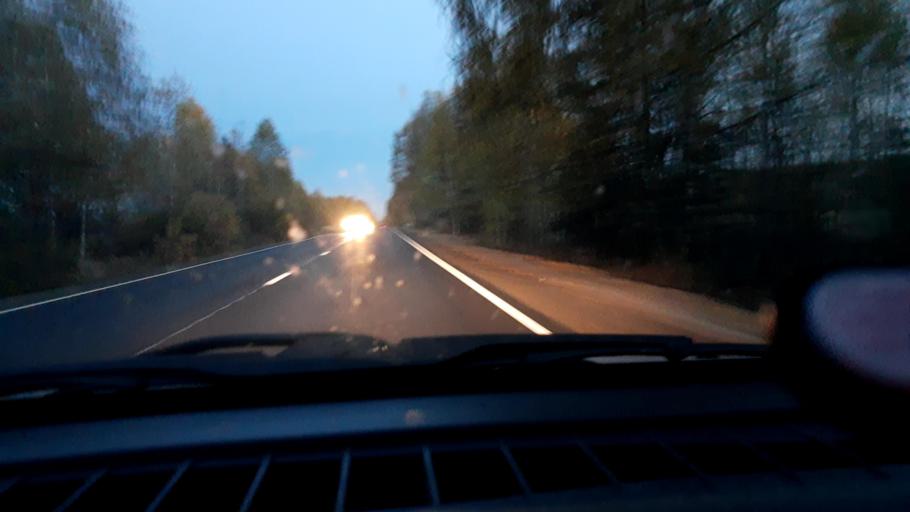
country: RU
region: Nizjnij Novgorod
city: Novaya Balakhna
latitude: 56.5667
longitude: 43.7178
